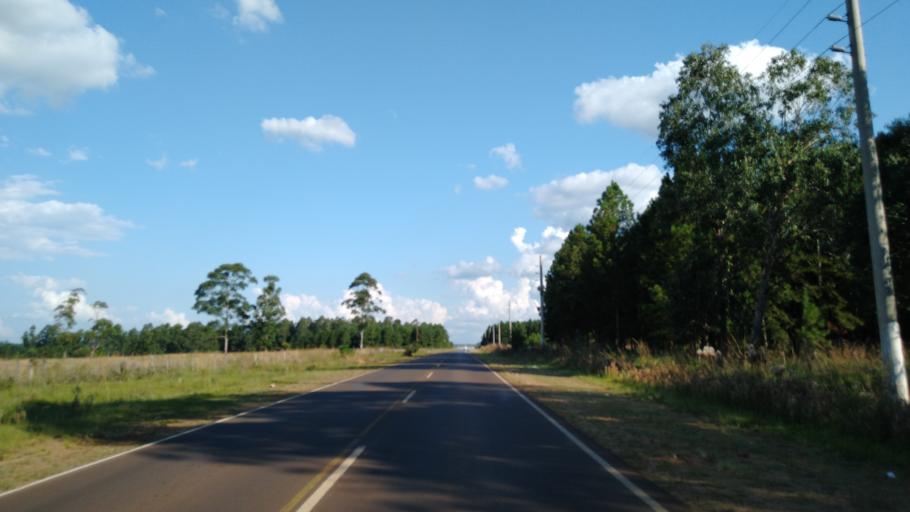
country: PY
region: Itapua
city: San Juan del Parana
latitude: -27.3786
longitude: -55.9919
